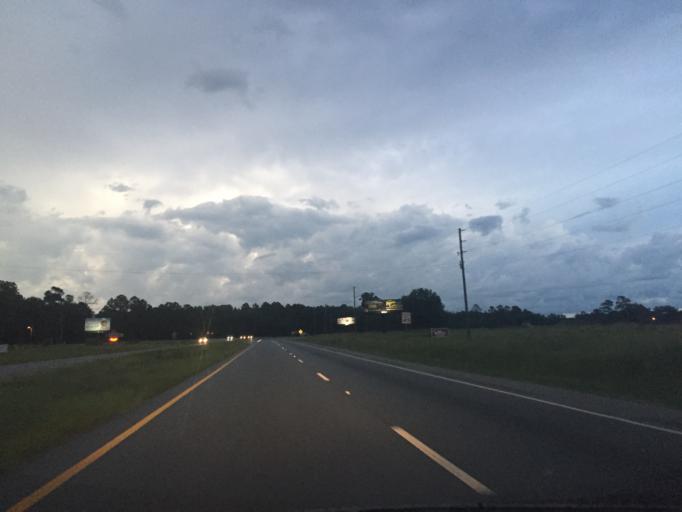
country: US
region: Georgia
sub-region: Liberty County
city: Hinesville
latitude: 31.8237
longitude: -81.5191
